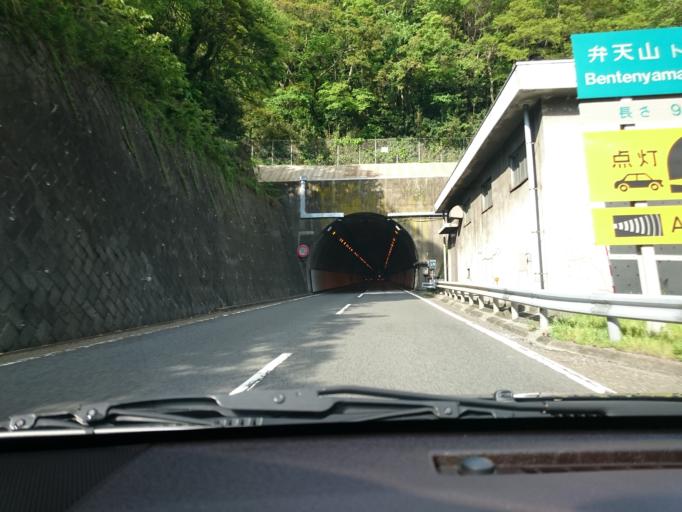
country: JP
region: Kanagawa
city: Ninomiya
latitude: 35.2919
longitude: 139.2037
